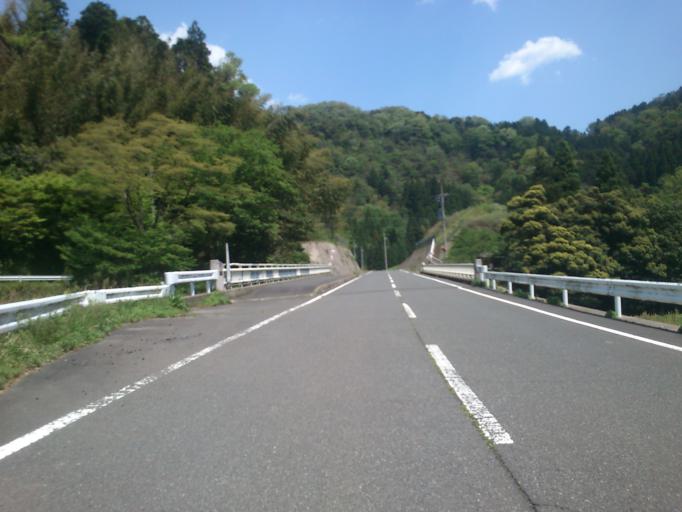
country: JP
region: Kyoto
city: Miyazu
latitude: 35.7285
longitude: 135.1627
